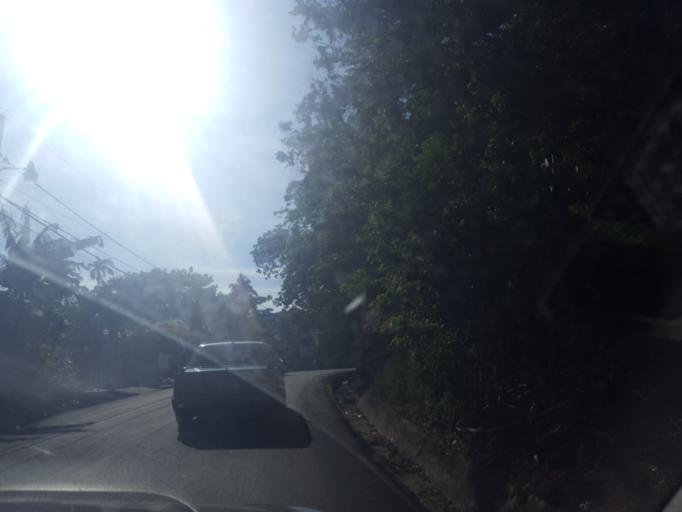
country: DO
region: La Vega
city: Rio Verde Arriba
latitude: 19.3473
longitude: -70.6245
